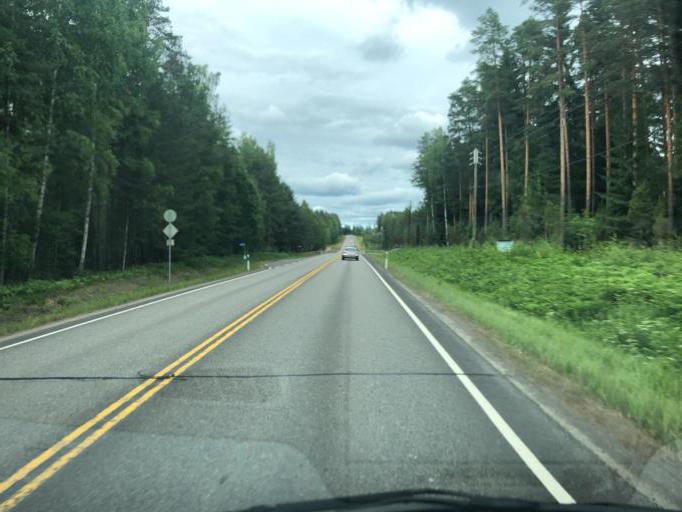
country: FI
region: Kymenlaakso
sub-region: Kouvola
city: Kouvola
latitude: 60.9689
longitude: 26.8893
